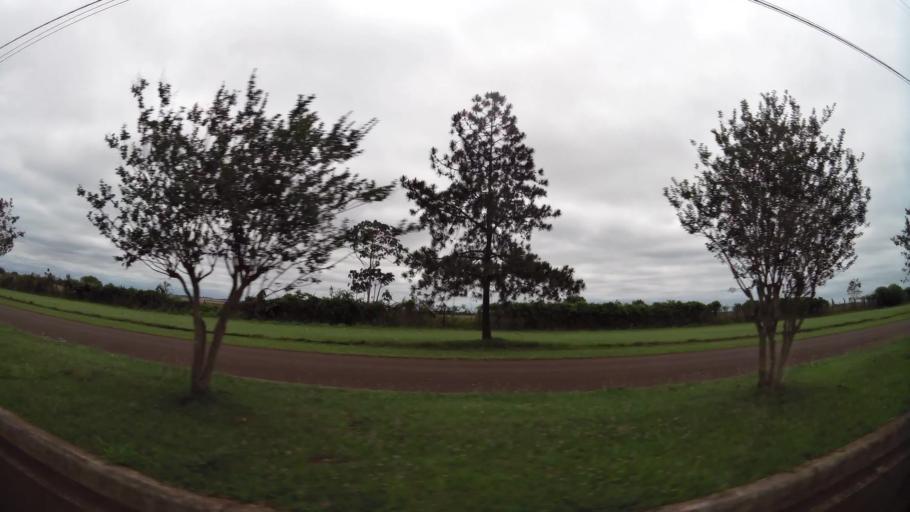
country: PY
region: Alto Parana
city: Colonia Yguazu
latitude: -25.4733
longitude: -54.8567
